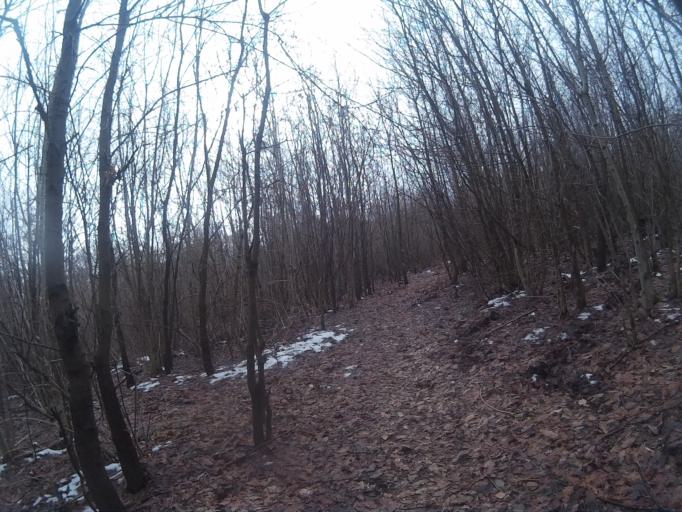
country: HU
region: Komarom-Esztergom
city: Tarjan
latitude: 47.6374
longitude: 18.4799
